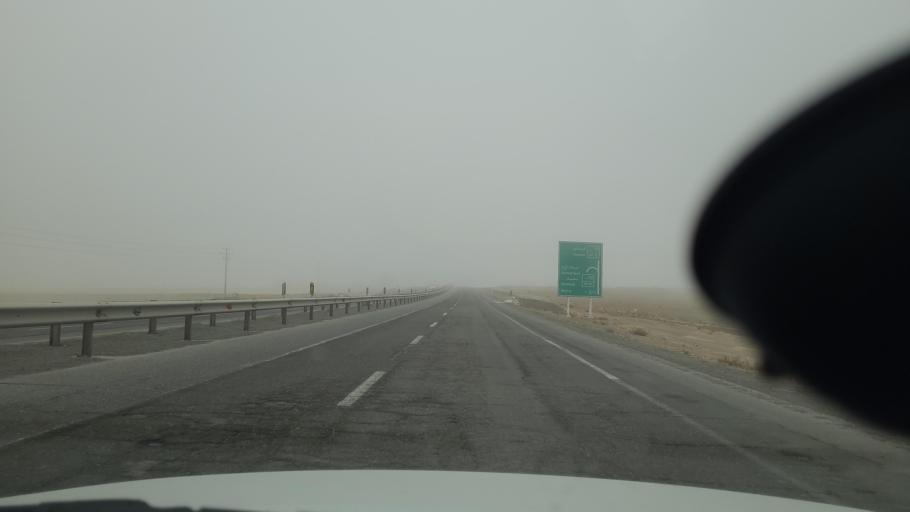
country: IR
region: Razavi Khorasan
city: Fariman
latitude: 35.7566
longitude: 59.7505
